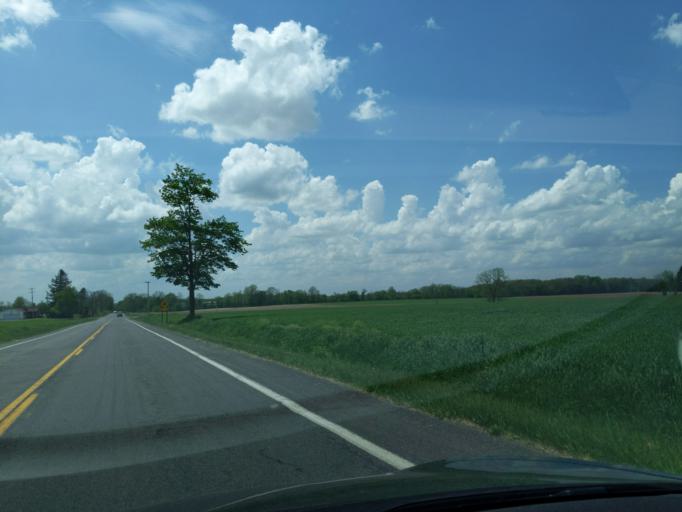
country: US
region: Michigan
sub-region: Ingham County
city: Mason
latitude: 42.5963
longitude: -84.3811
